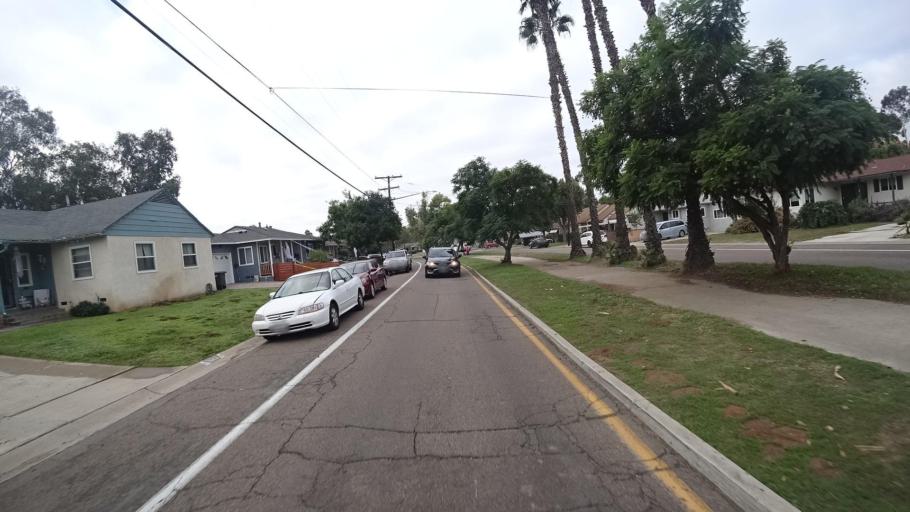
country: US
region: California
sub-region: San Diego County
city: Spring Valley
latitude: 32.7495
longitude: -117.0135
